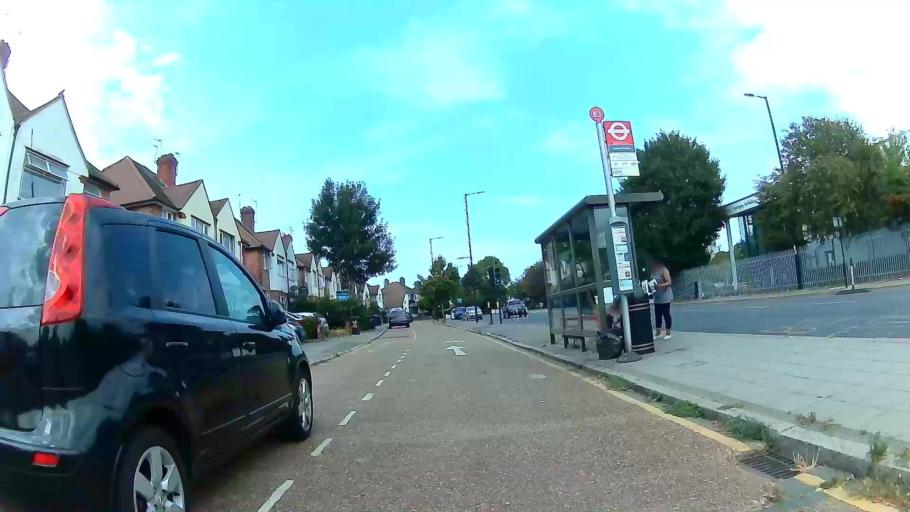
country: GB
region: England
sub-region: Greater London
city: Enfield
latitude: 51.6527
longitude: -0.0479
